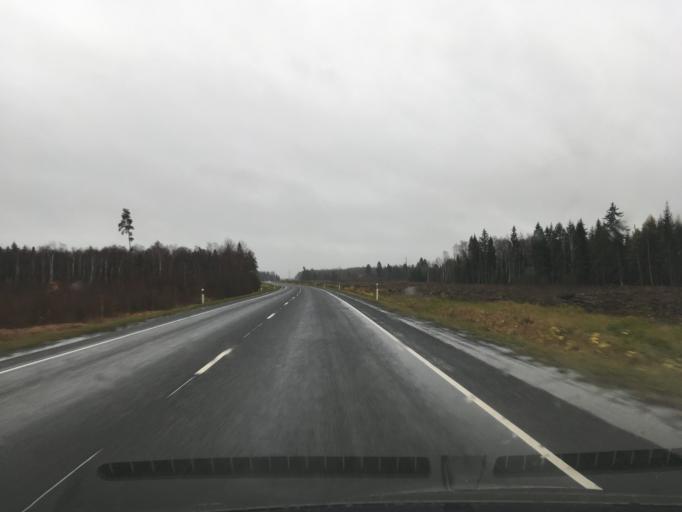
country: EE
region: Harju
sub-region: Nissi vald
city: Turba
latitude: 58.9453
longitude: 24.0854
